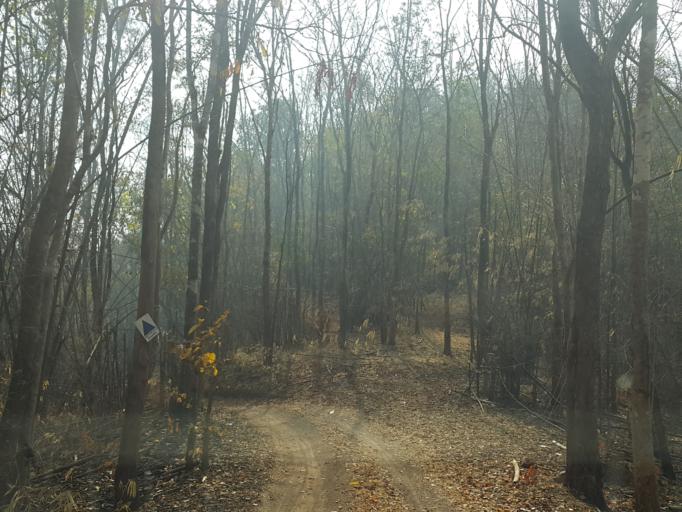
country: TH
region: Chiang Mai
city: Hang Dong
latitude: 18.7515
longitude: 98.8556
